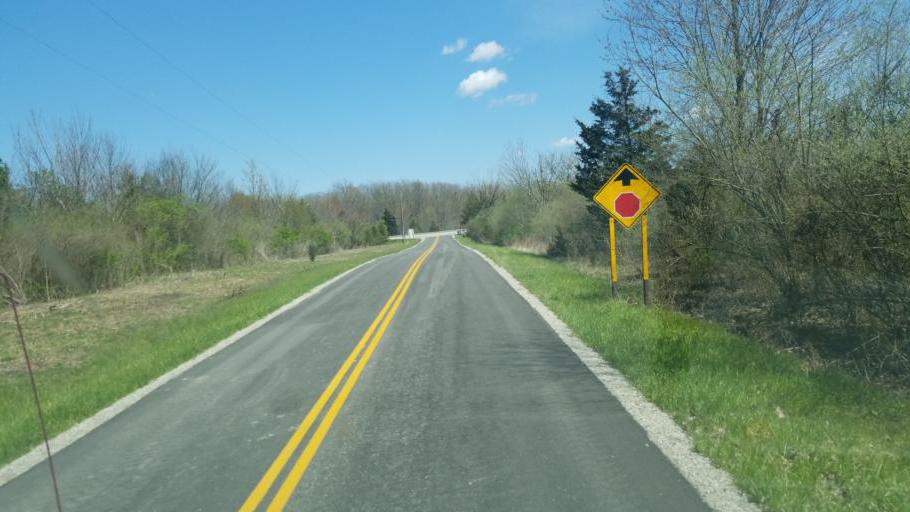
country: US
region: Ohio
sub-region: Delaware County
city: Delaware
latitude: 40.3730
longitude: -83.0760
